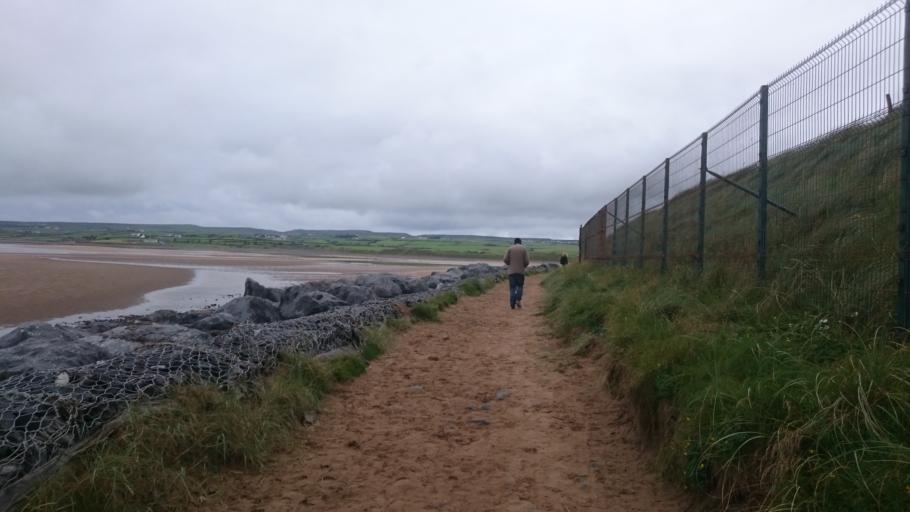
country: IE
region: Munster
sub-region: An Clar
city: Kilrush
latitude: 52.9390
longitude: -9.3562
